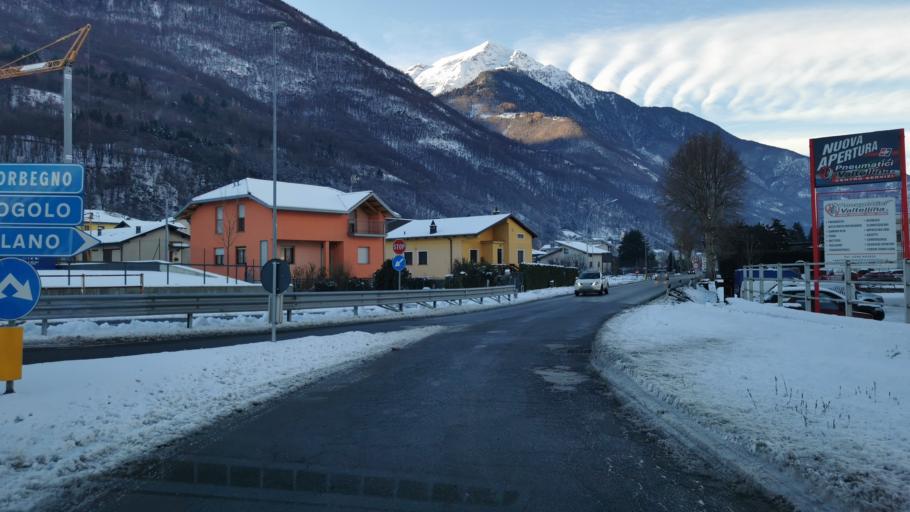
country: IT
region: Lombardy
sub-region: Provincia di Sondrio
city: Rogolo
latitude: 46.1376
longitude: 9.4877
